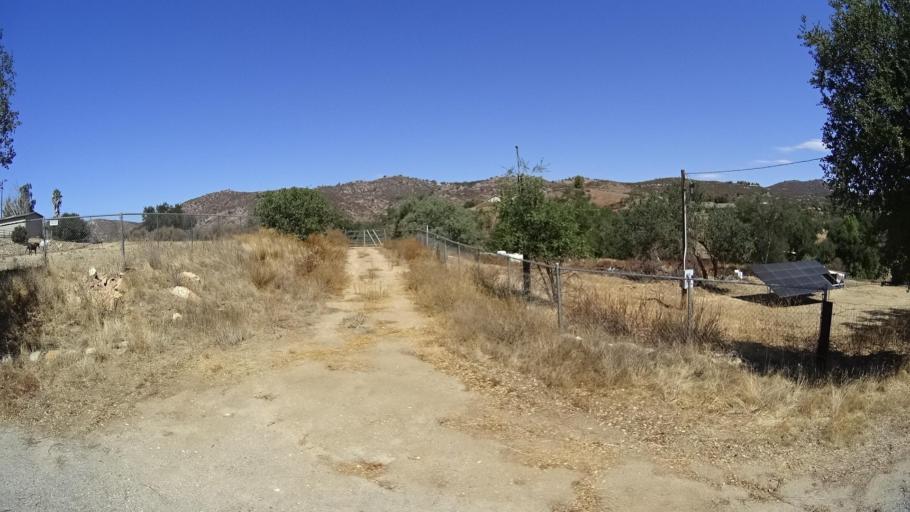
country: US
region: California
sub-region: San Diego County
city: San Diego Country Estates
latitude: 33.0493
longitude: -116.7872
